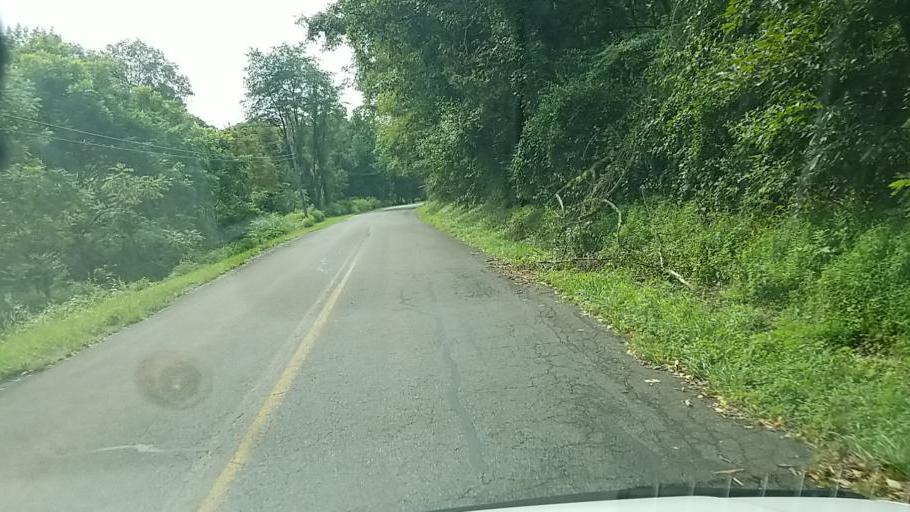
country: US
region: Pennsylvania
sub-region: Dauphin County
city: Matamoras
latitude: 40.5011
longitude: -76.8984
